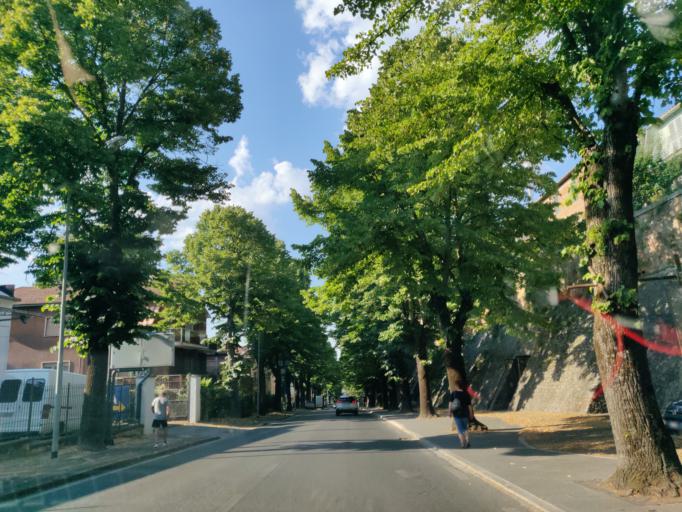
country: IT
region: Latium
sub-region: Provincia di Viterbo
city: Acquapendente
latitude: 42.7441
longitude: 11.8630
